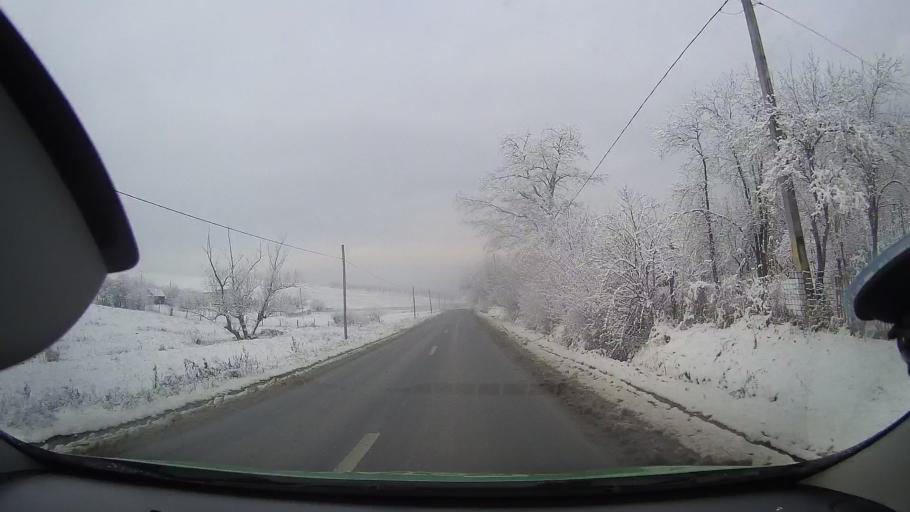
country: RO
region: Mures
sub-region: Comuna Atintis
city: Atintis
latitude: 46.4480
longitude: 24.0873
